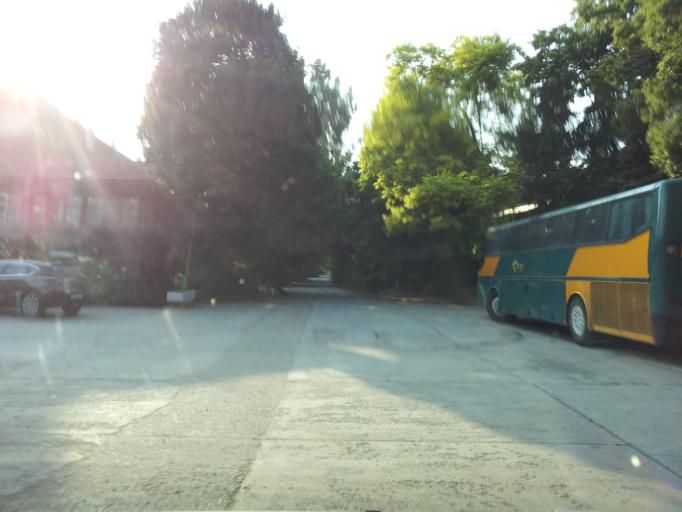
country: HU
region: Veszprem
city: Balatonkenese
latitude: 47.0183
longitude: 18.1480
